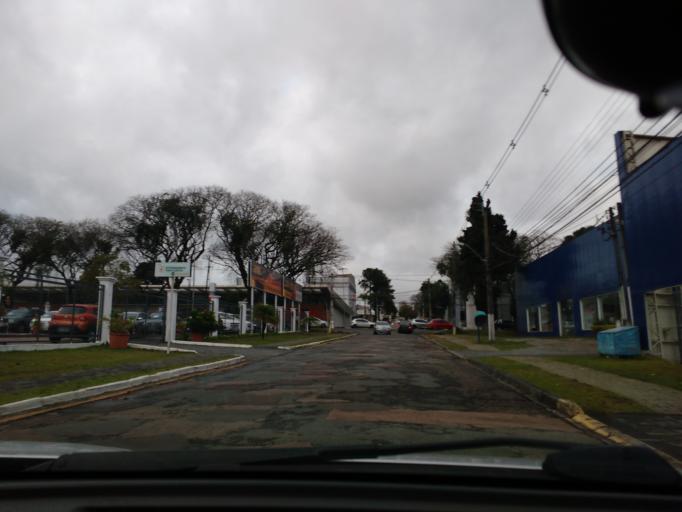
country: BR
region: Parana
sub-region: Pinhais
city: Pinhais
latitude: -25.4277
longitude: -49.2296
